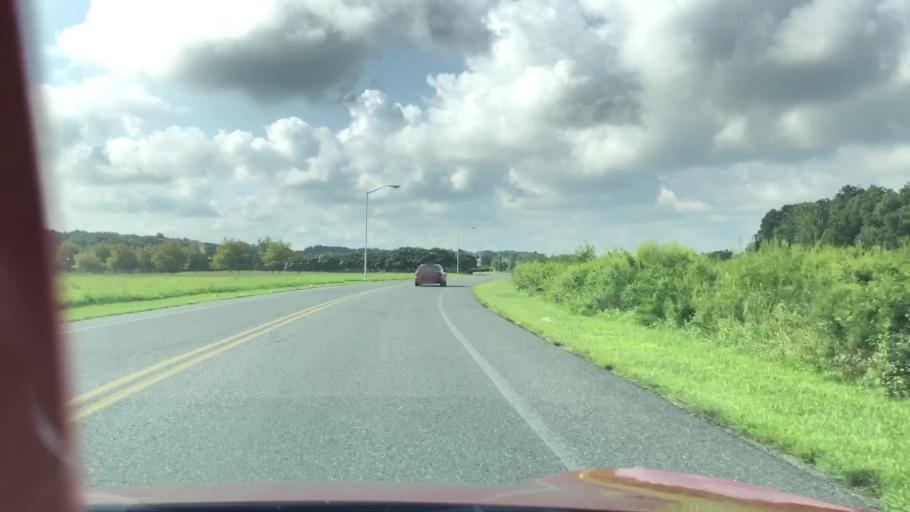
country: US
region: Maryland
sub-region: Wicomico County
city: Delmar
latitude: 38.4055
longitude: -75.5625
